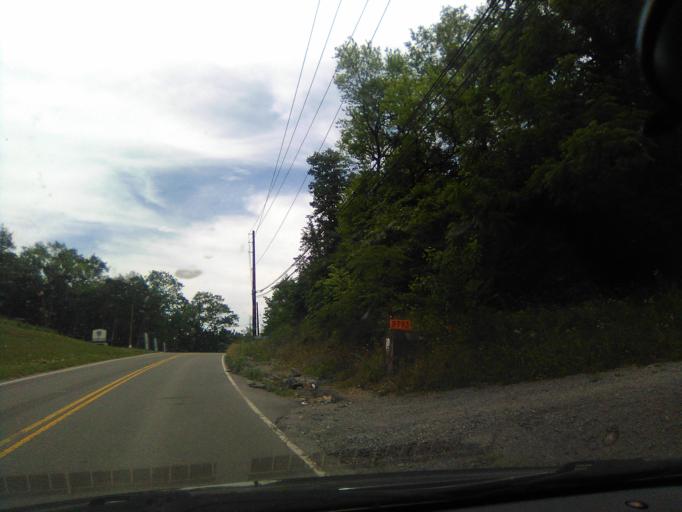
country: US
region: Tennessee
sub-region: Davidson County
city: Belle Meade
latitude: 36.1301
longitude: -86.9136
